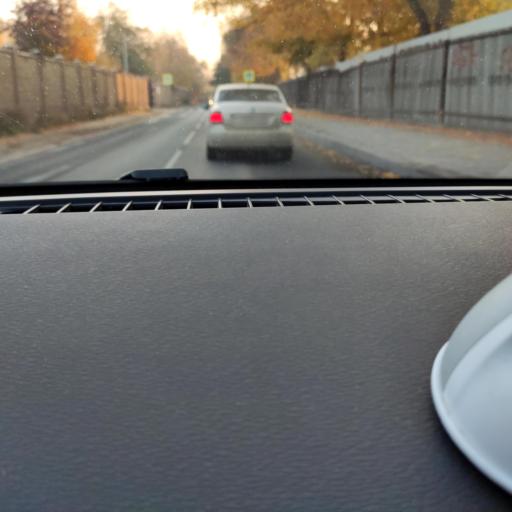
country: RU
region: Samara
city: Petra-Dubrava
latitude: 53.2389
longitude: 50.2694
